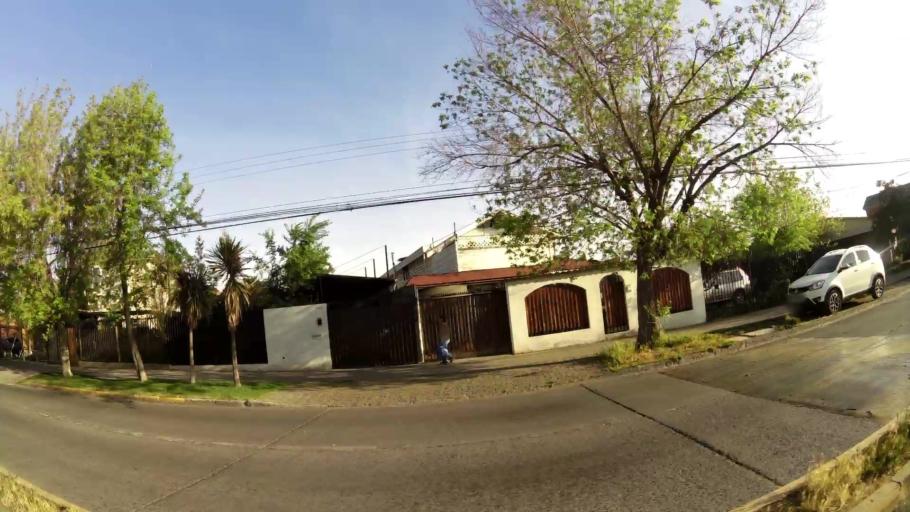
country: CL
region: Santiago Metropolitan
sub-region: Provincia de Cordillera
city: Puente Alto
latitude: -33.5437
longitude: -70.5736
